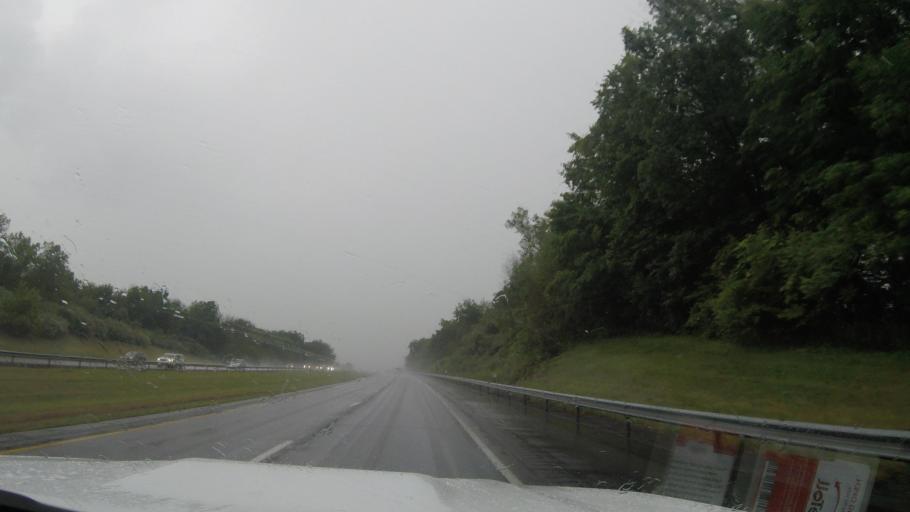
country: US
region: New York
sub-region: Ontario County
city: Phelps
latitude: 42.9559
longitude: -77.0234
